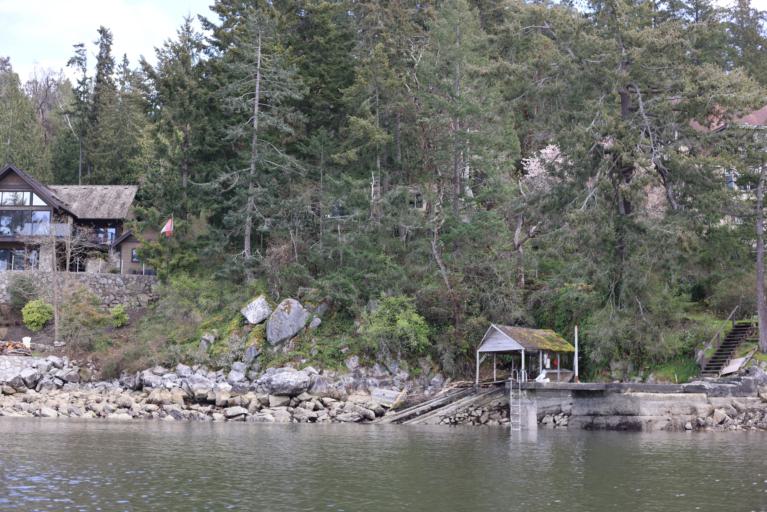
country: CA
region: British Columbia
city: North Saanich
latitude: 48.6073
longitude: -123.4817
